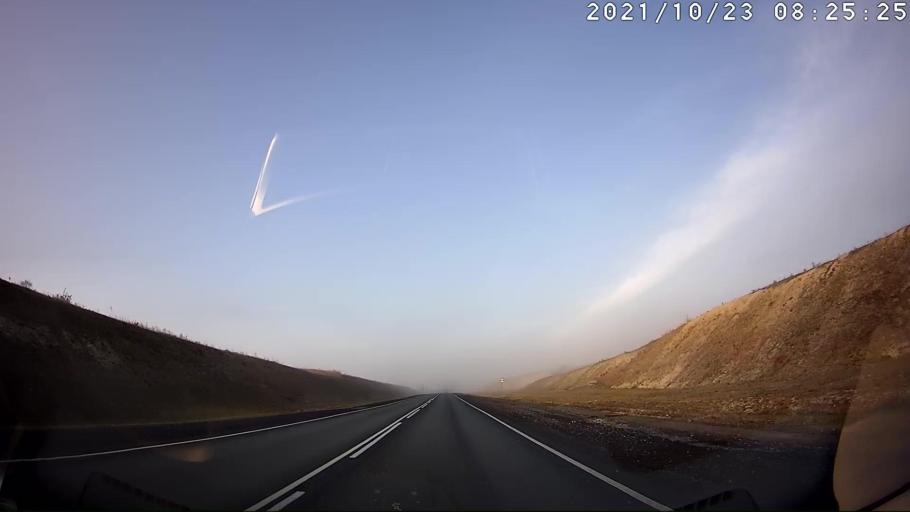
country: RU
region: Saratov
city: Sennoy
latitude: 52.1389
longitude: 46.8827
